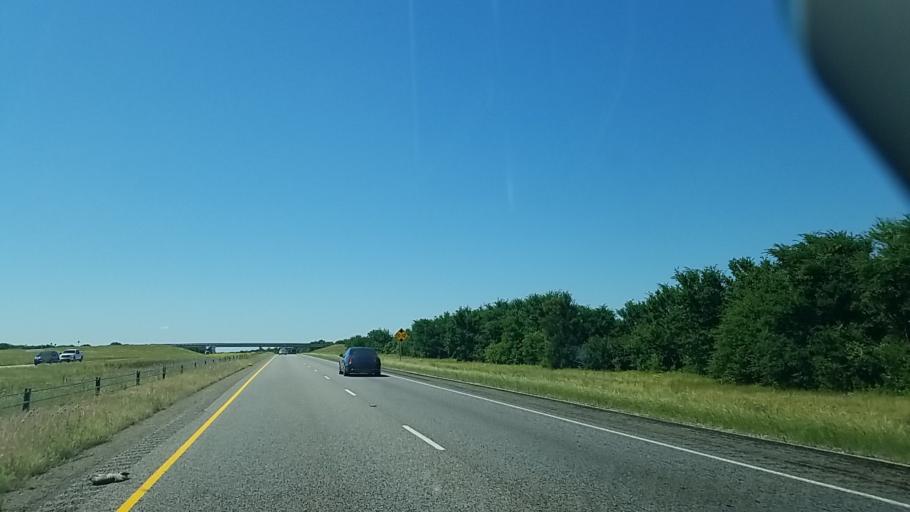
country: US
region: Texas
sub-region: Freestone County
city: Fairfield
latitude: 31.8261
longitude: -96.2811
